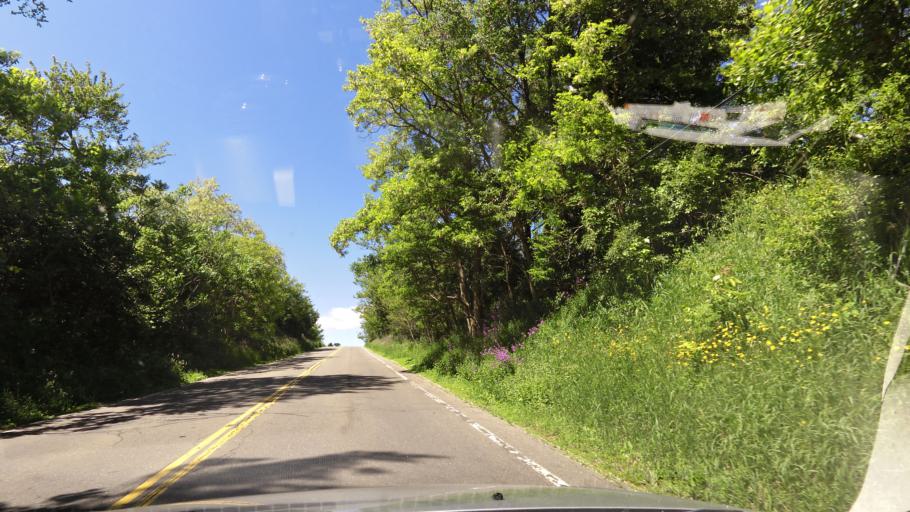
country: CA
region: Ontario
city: Newmarket
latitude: 43.9592
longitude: -79.5367
